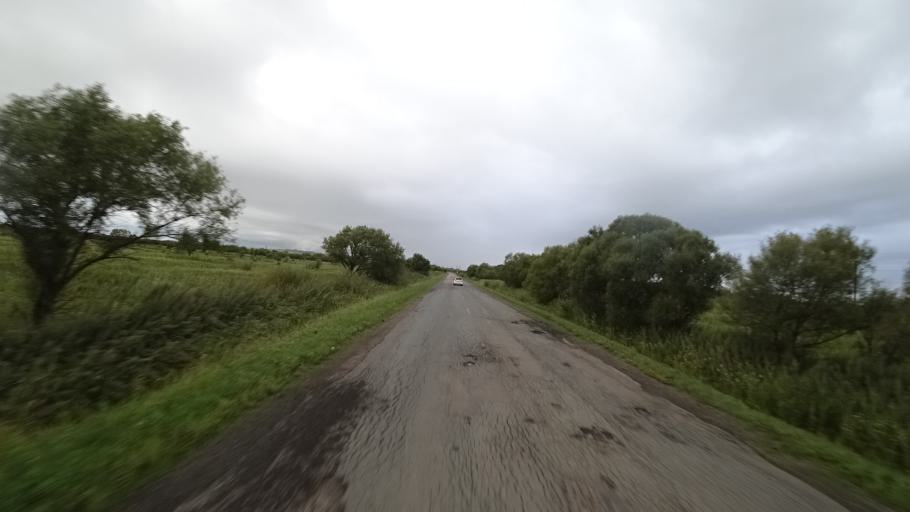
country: RU
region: Primorskiy
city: Chernigovka
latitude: 44.3600
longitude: 132.5567
